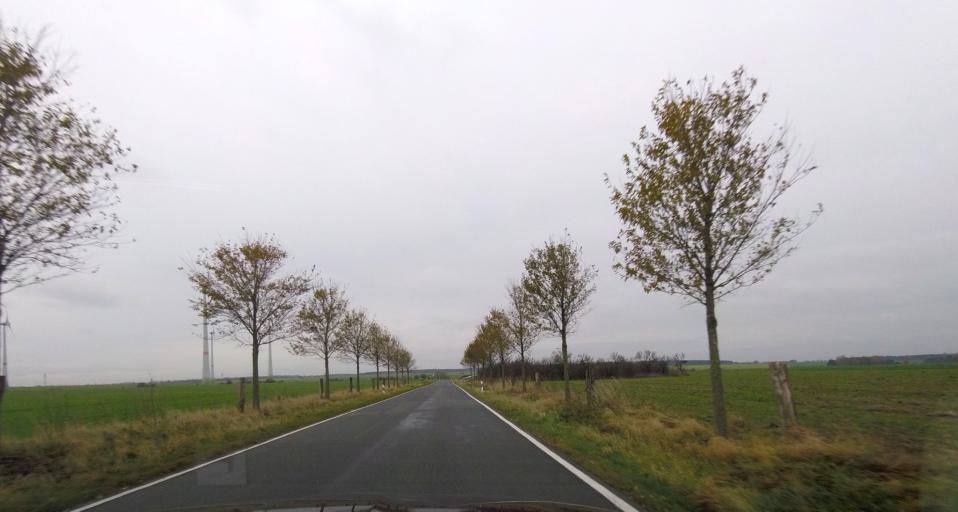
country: DE
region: Saxony-Anhalt
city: Kropstadt
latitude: 51.9892
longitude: 12.7951
